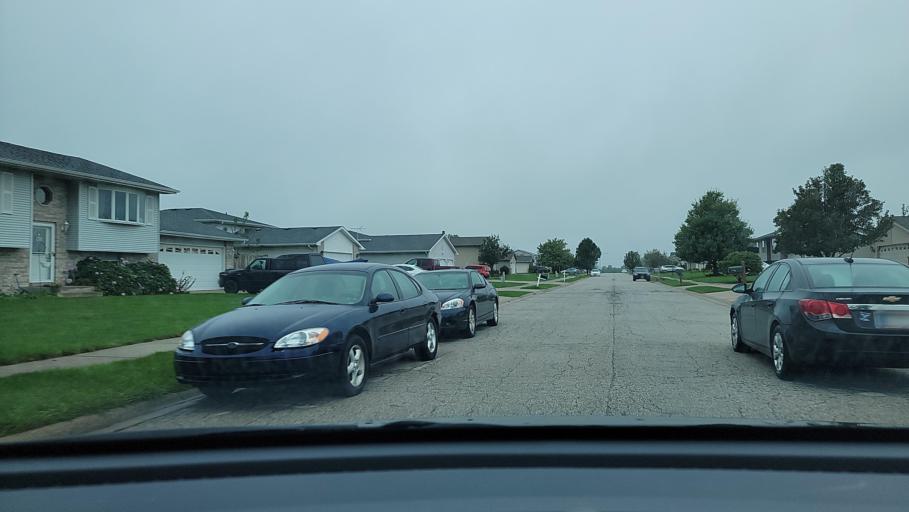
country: US
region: Indiana
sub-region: Porter County
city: Portage
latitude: 41.5420
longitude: -87.1929
